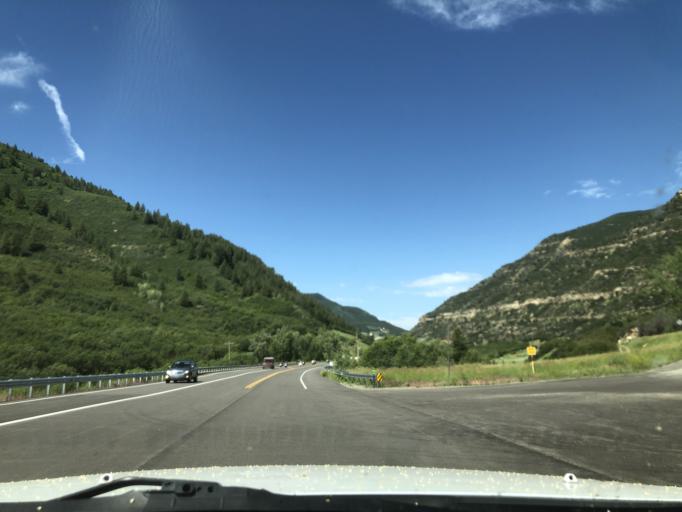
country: US
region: Colorado
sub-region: Delta County
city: Paonia
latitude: 38.9314
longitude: -107.4071
